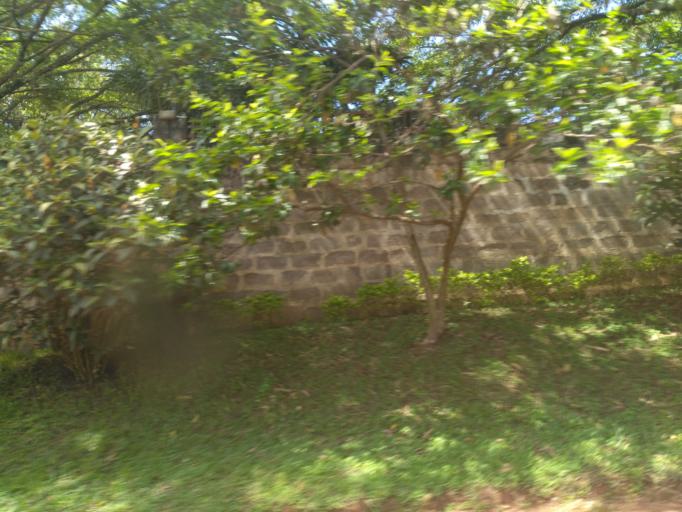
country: UG
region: Central Region
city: Kampala Central Division
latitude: 0.3297
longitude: 32.5798
